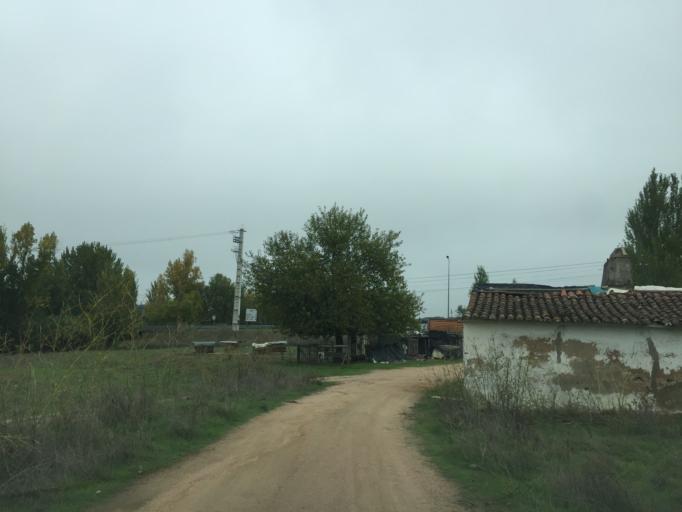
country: PT
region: Portalegre
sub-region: Arronches
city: Arronches
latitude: 39.0551
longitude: -7.4455
